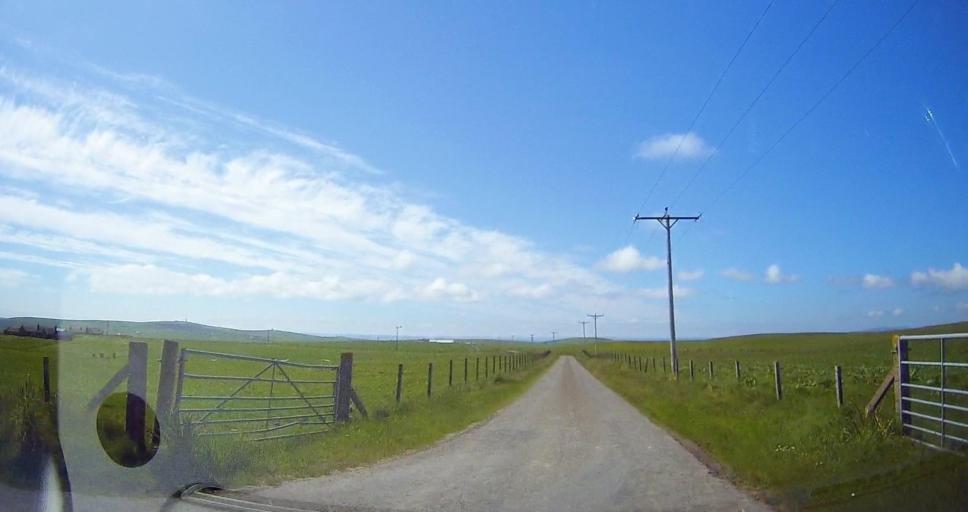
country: GB
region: Scotland
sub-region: Orkney Islands
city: Kirkwall
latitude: 58.8132
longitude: -2.9228
